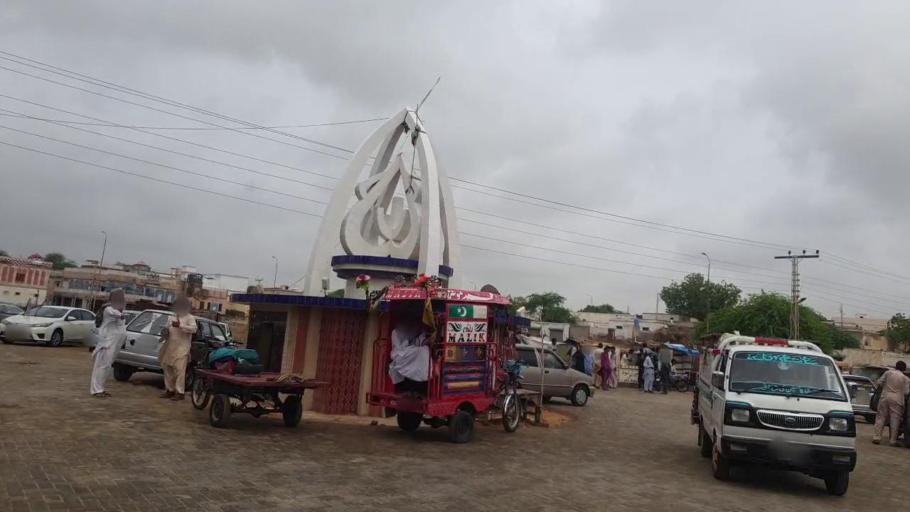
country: PK
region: Sindh
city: Diplo
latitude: 24.4690
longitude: 69.5795
